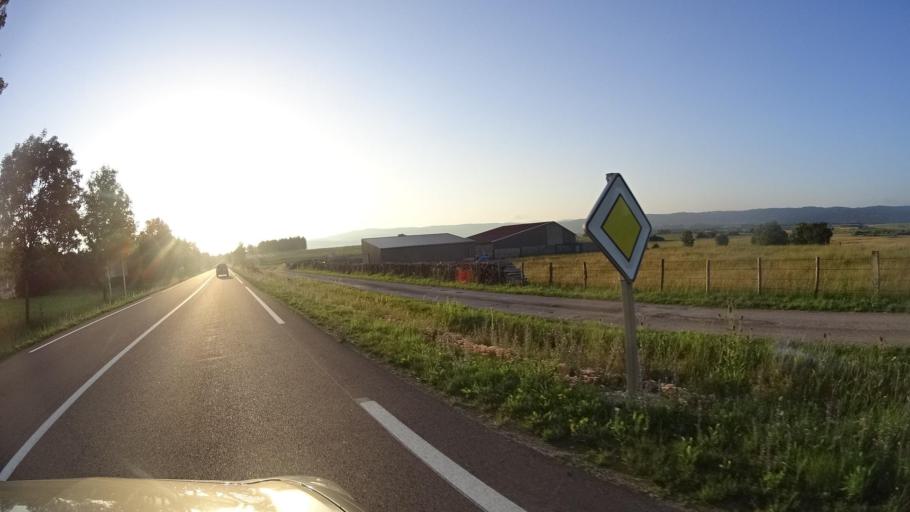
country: FR
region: Franche-Comte
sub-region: Departement du Doubs
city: Doubs
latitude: 46.9096
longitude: 6.2701
